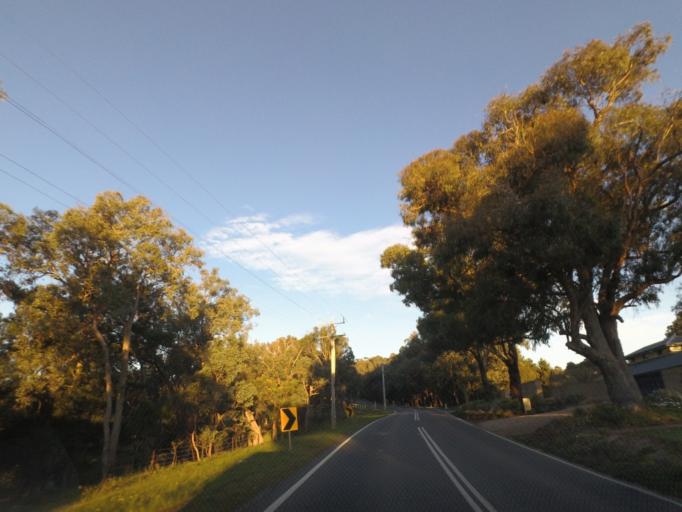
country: AU
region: Victoria
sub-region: Manningham
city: Warrandyte
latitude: -37.7381
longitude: 145.2547
